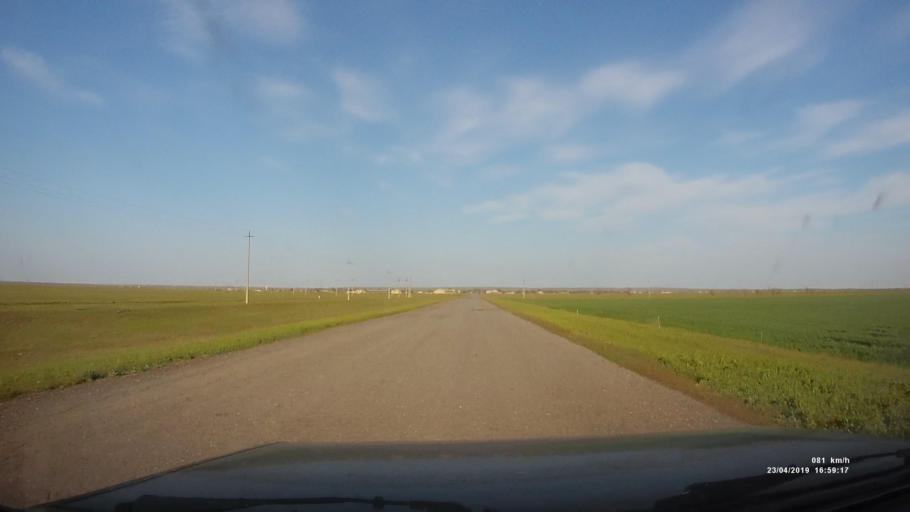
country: RU
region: Kalmykiya
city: Priyutnoye
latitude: 46.3082
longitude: 43.3866
